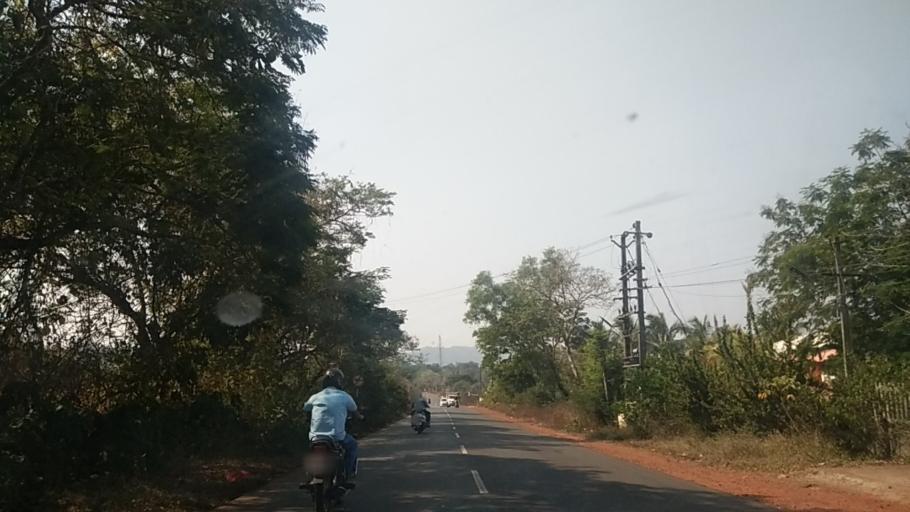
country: IN
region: Goa
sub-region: North Goa
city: Dicholi
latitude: 15.5824
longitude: 73.9663
